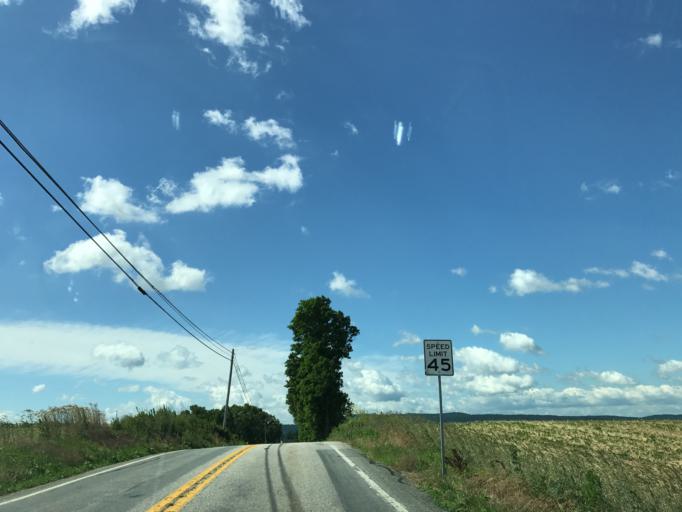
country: US
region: Pennsylvania
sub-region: Lancaster County
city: Maytown
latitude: 40.0963
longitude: -76.5908
